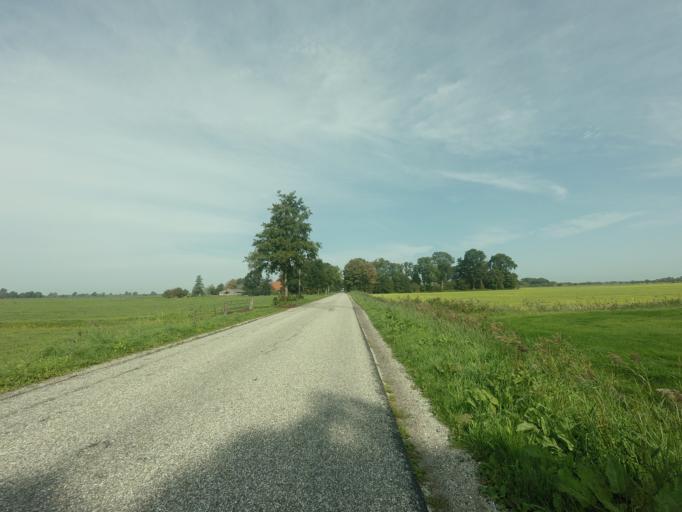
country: NL
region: Groningen
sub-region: Gemeente Leek
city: Leek
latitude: 53.1974
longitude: 6.3524
